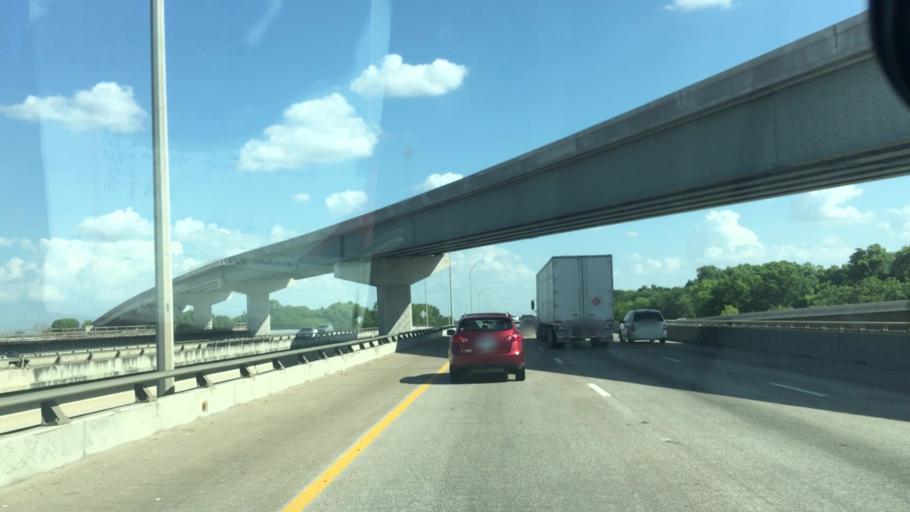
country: US
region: Texas
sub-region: Dallas County
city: Dallas
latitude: 32.7480
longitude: -96.7695
